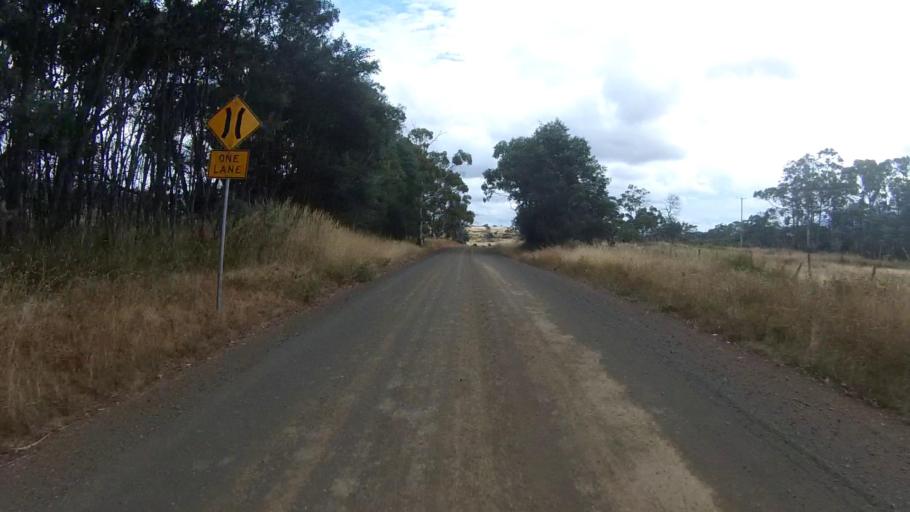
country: AU
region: Tasmania
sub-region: Break O'Day
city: St Helens
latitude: -41.8262
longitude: 147.9798
